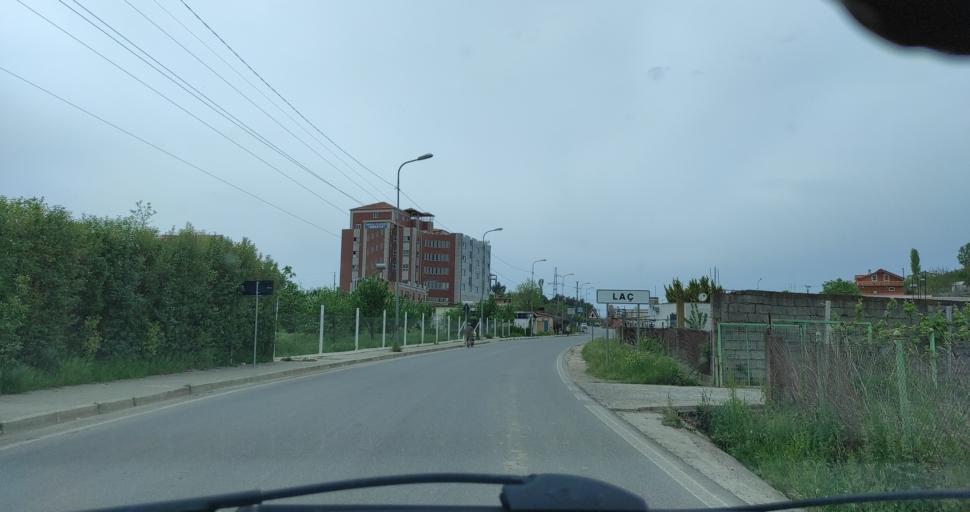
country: AL
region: Lezhe
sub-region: Rrethi i Kurbinit
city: Lac
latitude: 41.6202
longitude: 19.7098
